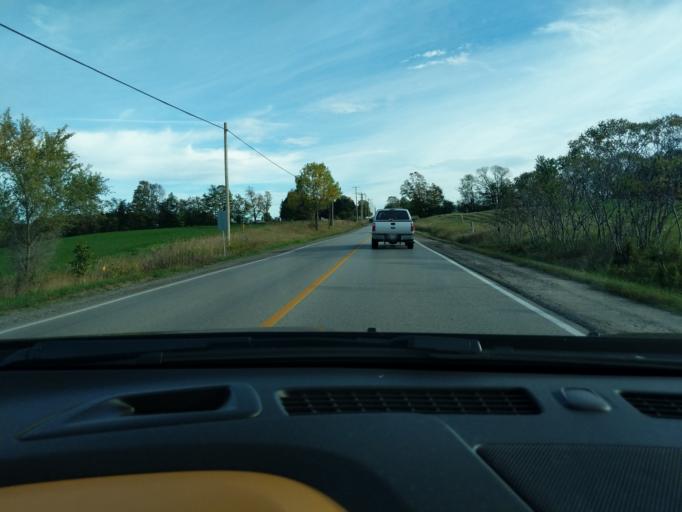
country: CA
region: Ontario
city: Barrie
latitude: 44.4224
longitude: -79.7604
